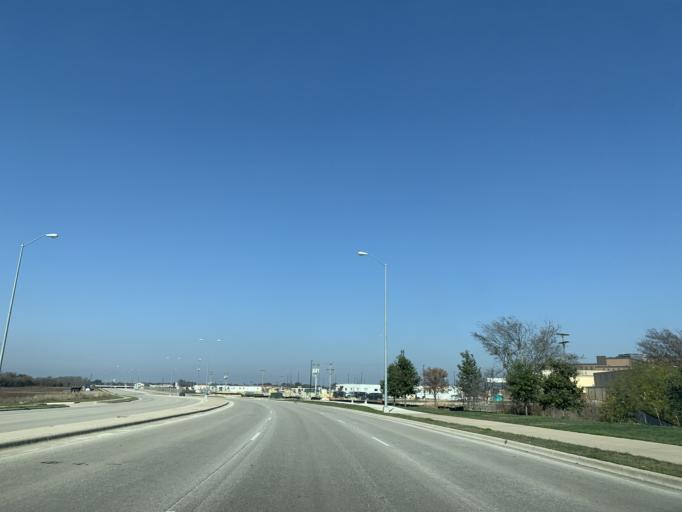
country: US
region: Texas
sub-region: Williamson County
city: Round Rock
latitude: 30.5151
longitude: -97.6365
